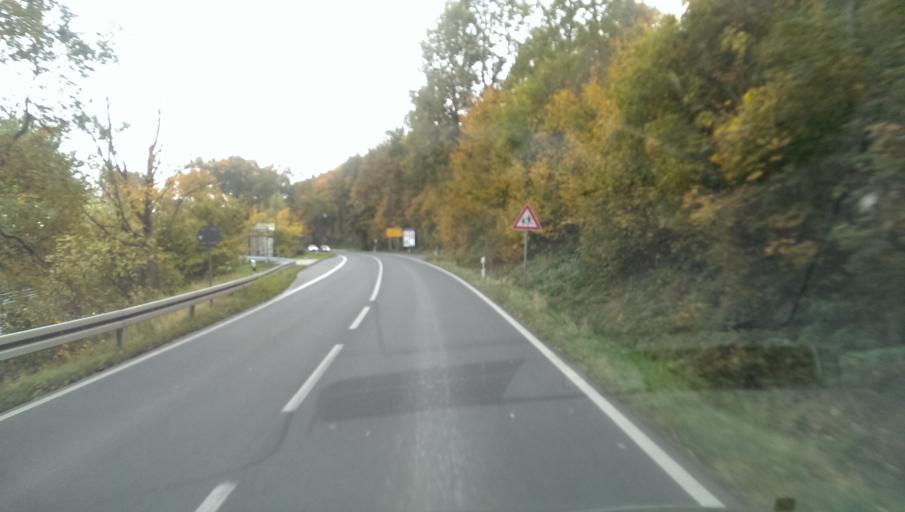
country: DE
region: Saxony
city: Rammenau
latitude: 51.1711
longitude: 14.1407
